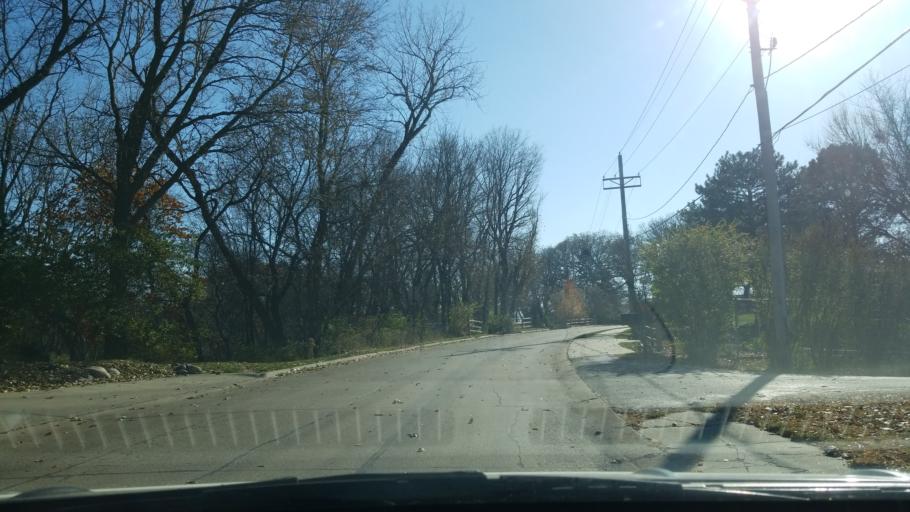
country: US
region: Nebraska
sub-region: Sarpy County
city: Bellevue
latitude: 41.1609
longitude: -95.9022
